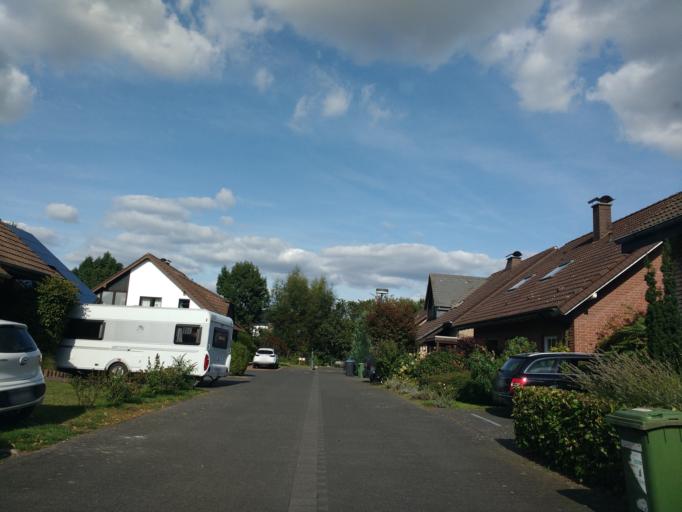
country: DE
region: North Rhine-Westphalia
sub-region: Regierungsbezirk Detmold
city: Hovelhof
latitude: 51.7429
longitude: 8.6784
